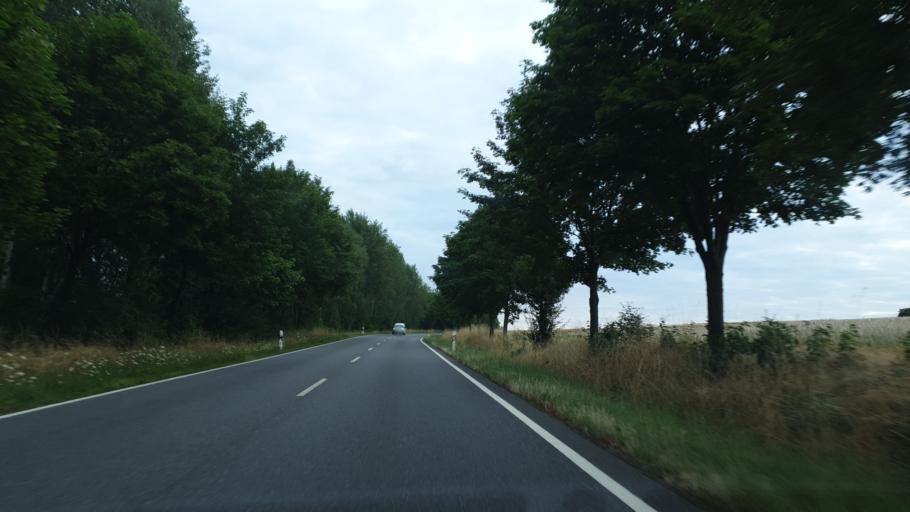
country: DE
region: Saxony
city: Sankt Egidien
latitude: 50.8039
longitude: 12.6254
